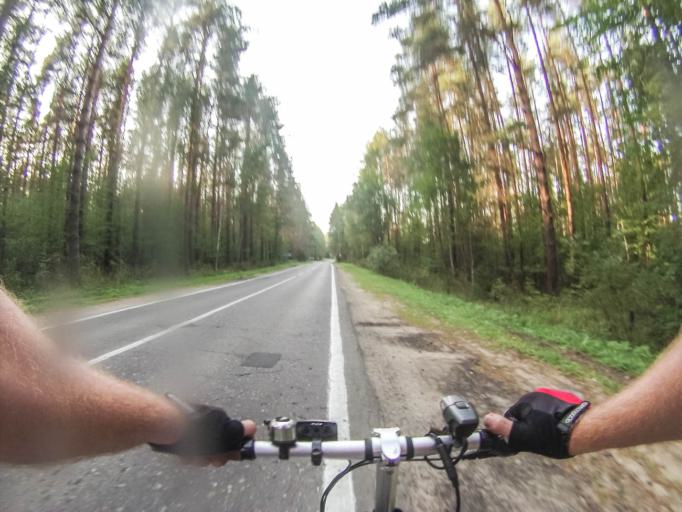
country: RU
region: Jaroslavl
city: Myshkin
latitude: 57.7659
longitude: 38.4434
